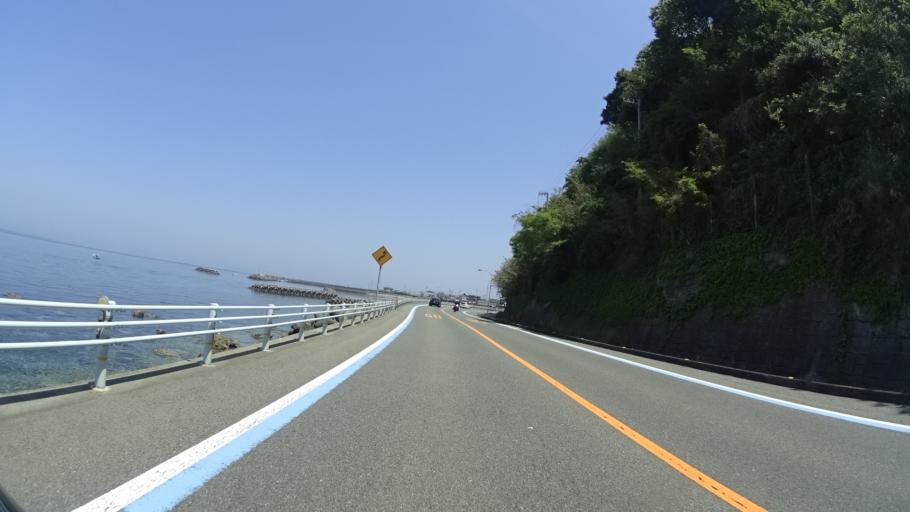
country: JP
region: Ehime
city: Ozu
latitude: 33.6052
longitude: 132.4730
